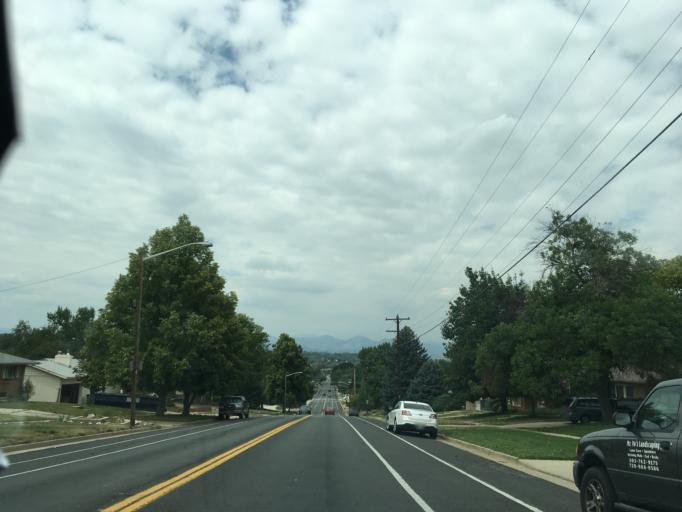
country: US
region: Colorado
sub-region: Arapahoe County
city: Sheridan
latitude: 39.6606
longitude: -105.0403
